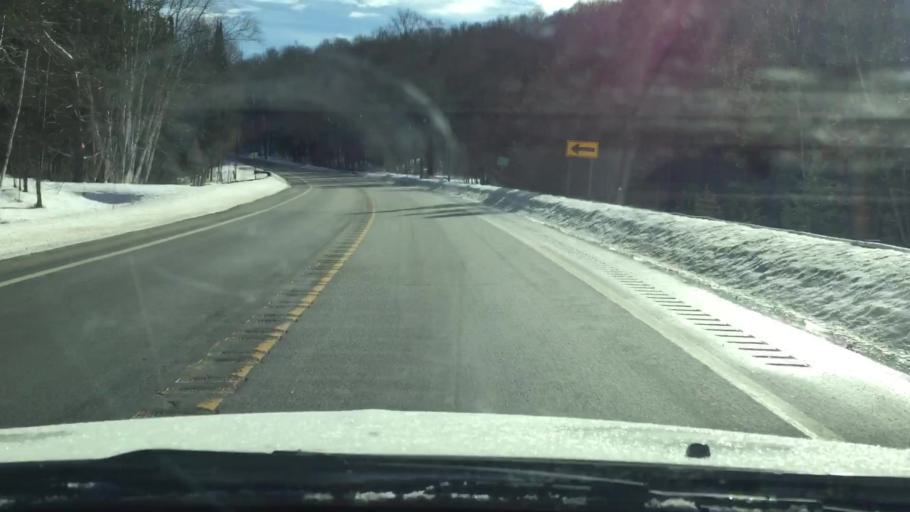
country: US
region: Michigan
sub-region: Antrim County
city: Mancelona
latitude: 45.0011
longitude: -85.0631
